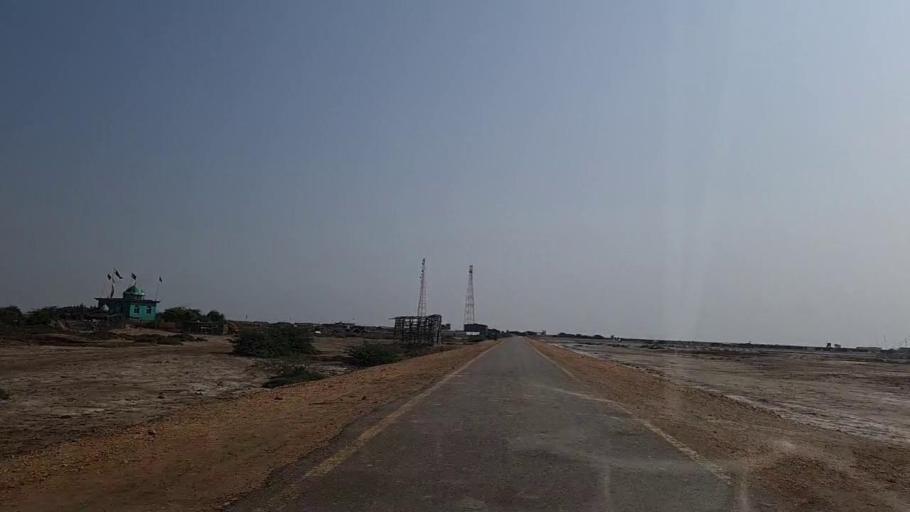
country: PK
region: Sindh
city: Chuhar Jamali
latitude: 24.1677
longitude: 67.8968
